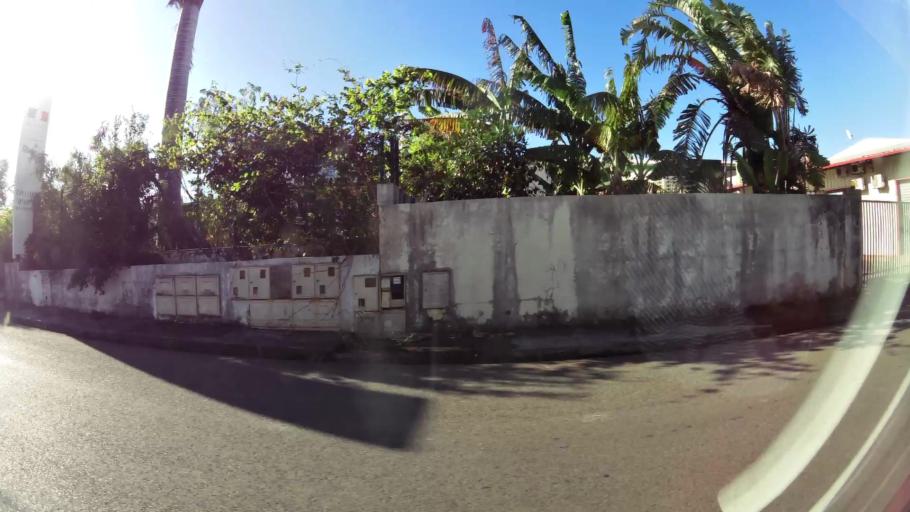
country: YT
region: Mamoudzou
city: Mamoudzou
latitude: -12.7660
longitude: 45.2283
